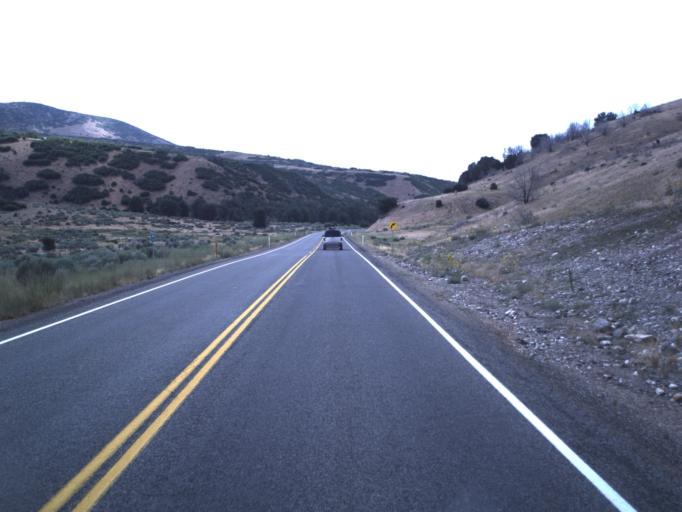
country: US
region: Utah
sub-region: Sanpete County
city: Fountain Green
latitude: 39.7026
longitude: -111.7030
